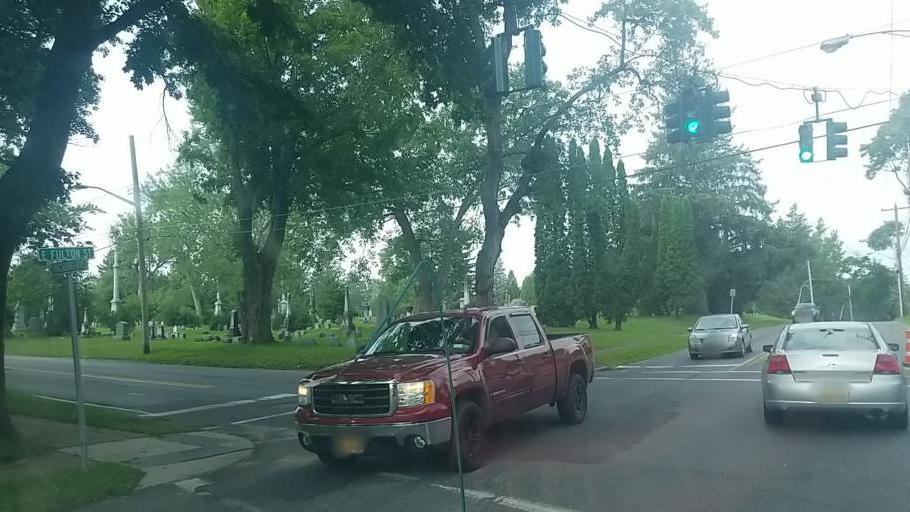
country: US
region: New York
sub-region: Fulton County
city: Gloversville
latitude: 43.0508
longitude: -74.3332
